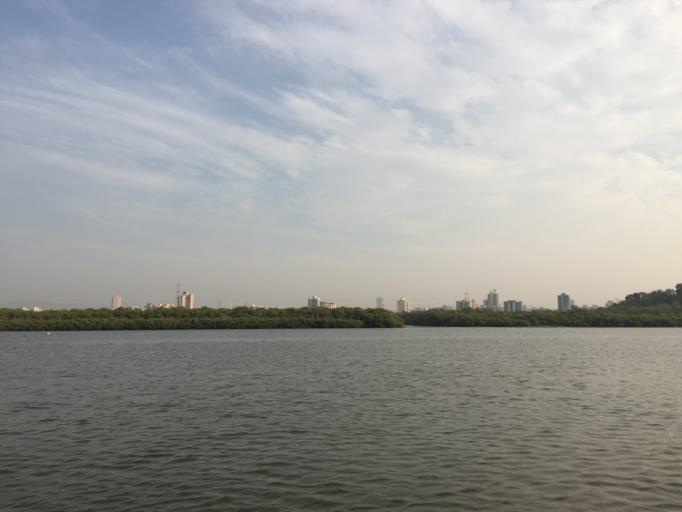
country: IN
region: Maharashtra
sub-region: Mumbai Suburban
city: Borivli
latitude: 19.2263
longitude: 72.8136
